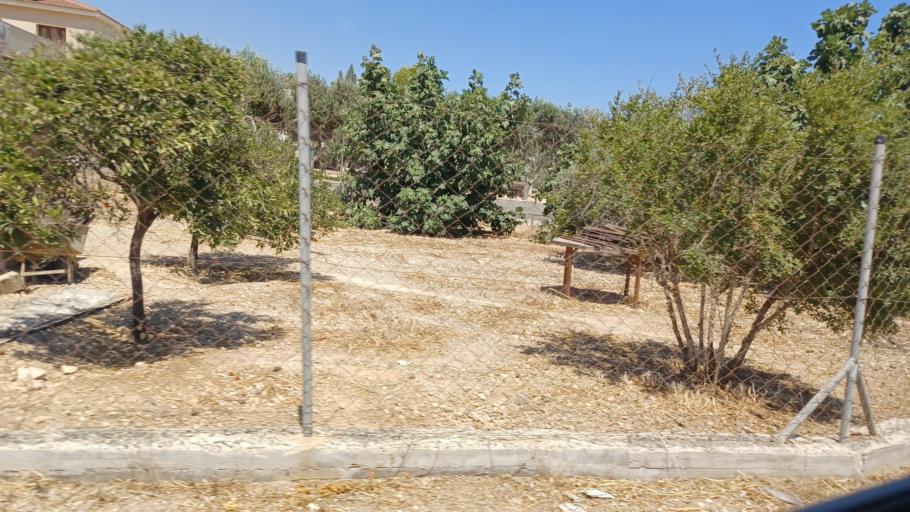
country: CY
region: Ammochostos
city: Acheritou
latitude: 35.0747
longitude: 33.8856
